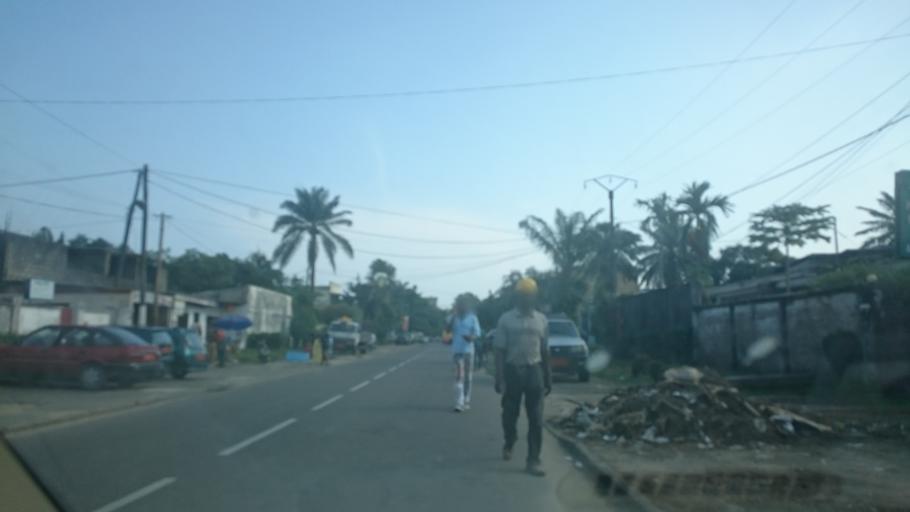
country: CM
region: Littoral
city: Douala
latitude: 4.0287
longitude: 9.6993
